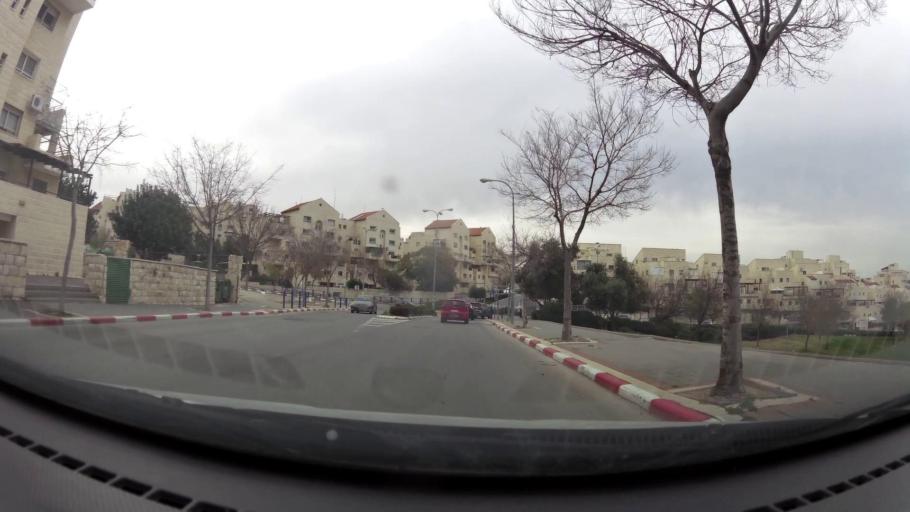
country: IL
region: Jerusalem
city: Bet Shemesh
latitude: 31.7109
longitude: 34.9972
